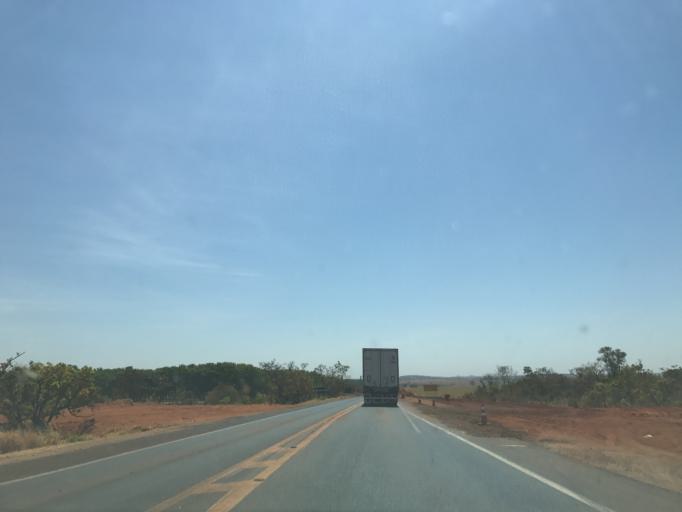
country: BR
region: Minas Gerais
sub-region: Prata
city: Prata
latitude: -19.4697
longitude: -48.8725
